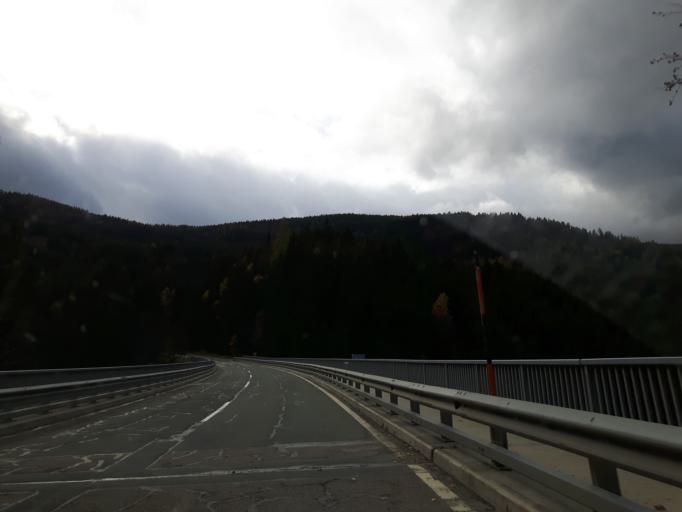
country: AT
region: Styria
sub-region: Politischer Bezirk Deutschlandsberg
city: Soboth
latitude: 46.7034
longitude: 15.0939
